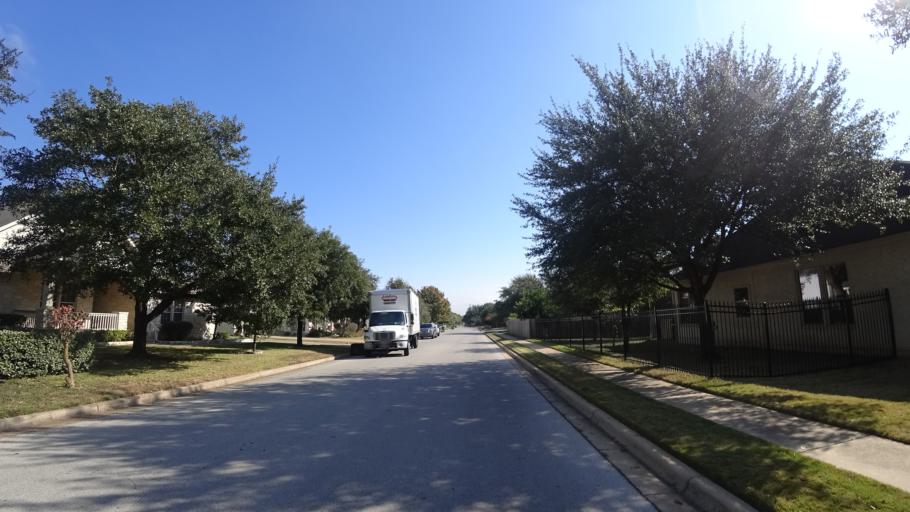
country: US
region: Texas
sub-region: Travis County
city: Shady Hollow
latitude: 30.1725
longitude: -97.8730
